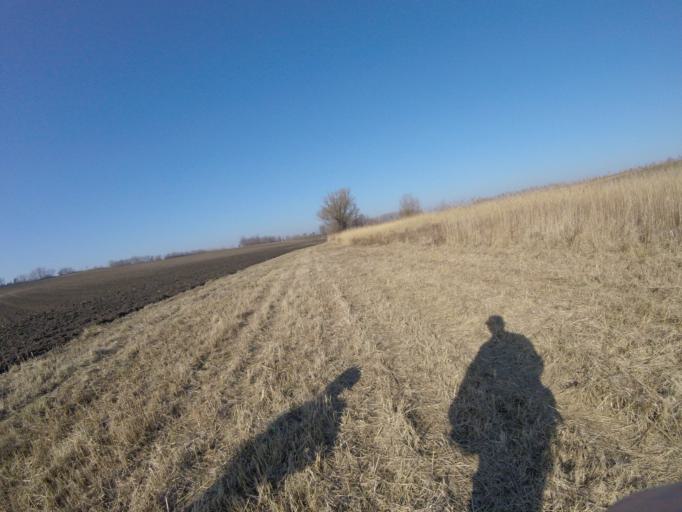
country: HU
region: Komarom-Esztergom
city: Csaszar
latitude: 47.5332
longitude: 18.1892
